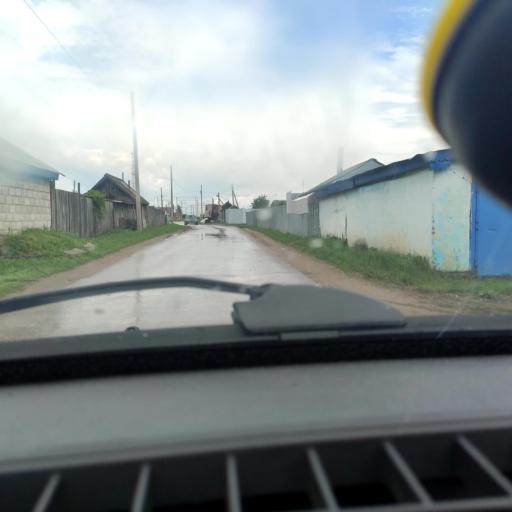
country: RU
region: Samara
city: Povolzhskiy
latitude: 53.6426
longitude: 49.6858
